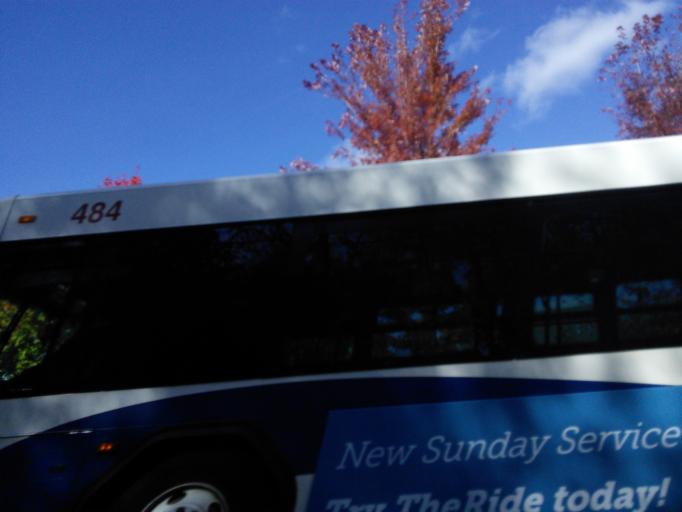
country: US
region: Michigan
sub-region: Washtenaw County
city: Ann Arbor
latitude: 42.2746
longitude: -83.7745
